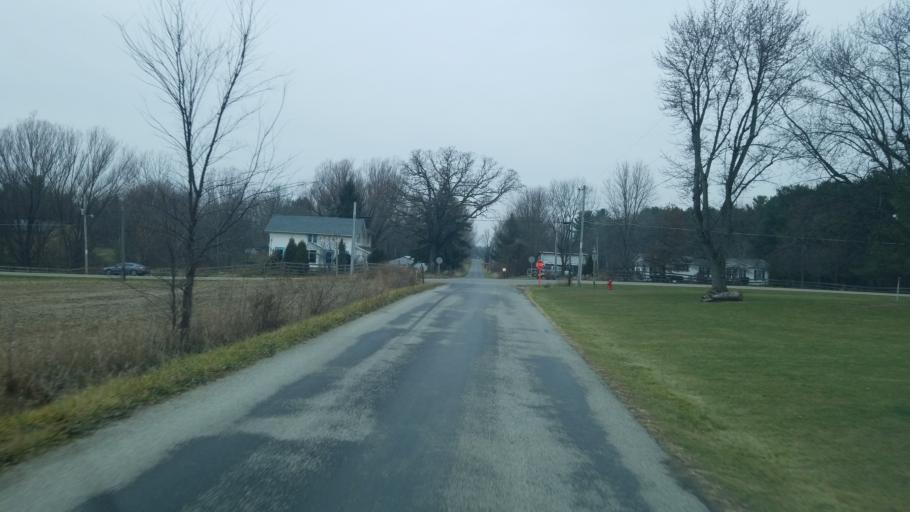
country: US
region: Ohio
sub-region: Morrow County
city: Cardington
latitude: 40.4329
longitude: -82.8235
